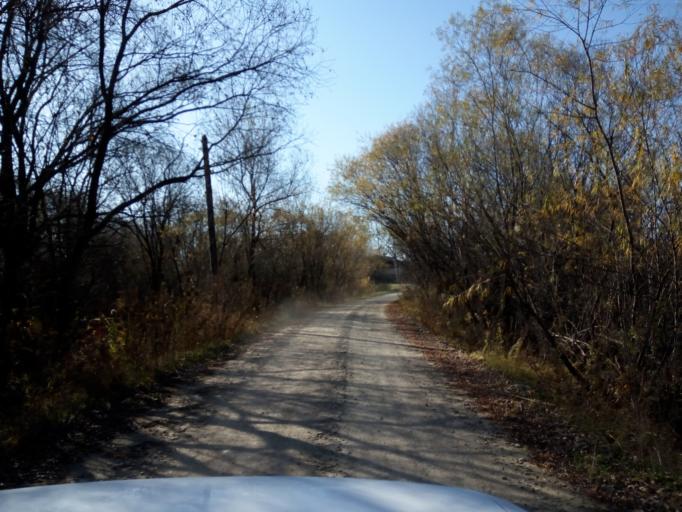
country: RU
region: Primorskiy
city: Dal'nerechensk
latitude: 45.9134
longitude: 133.8050
